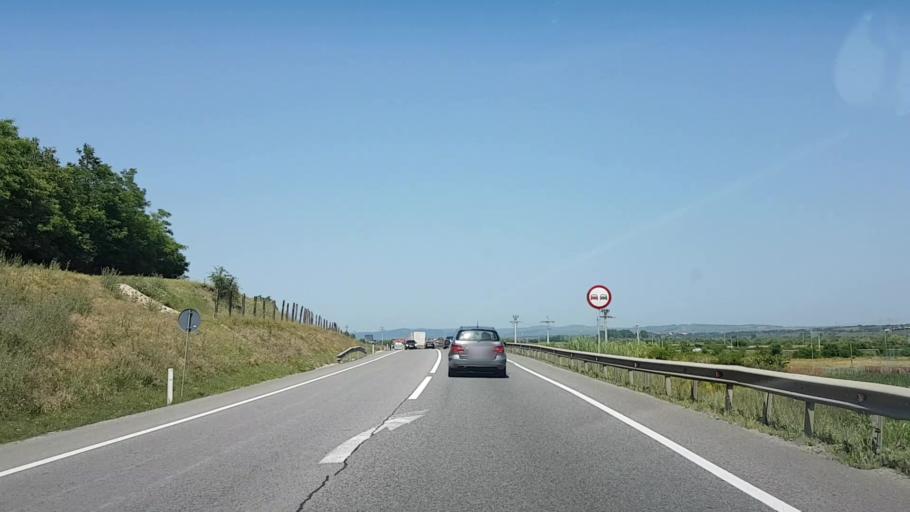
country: RO
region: Cluj
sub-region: Comuna Apahida
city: Apahida
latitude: 46.8190
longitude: 23.7419
